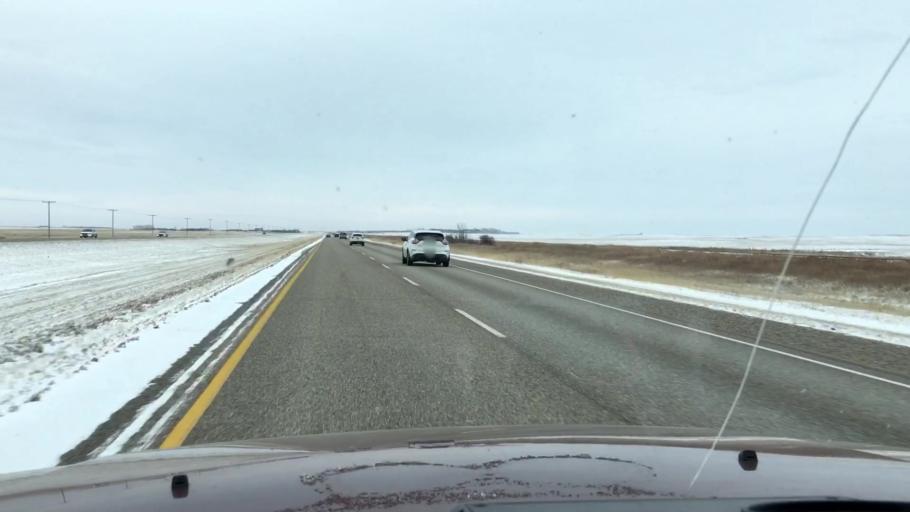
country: CA
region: Saskatchewan
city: Moose Jaw
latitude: 50.9955
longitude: -105.7584
